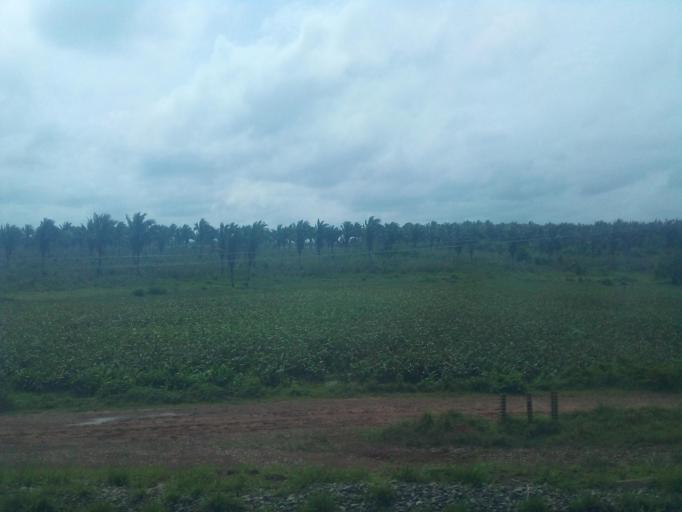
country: BR
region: Maranhao
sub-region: Arari
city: Arari
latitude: -3.4827
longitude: -44.6057
